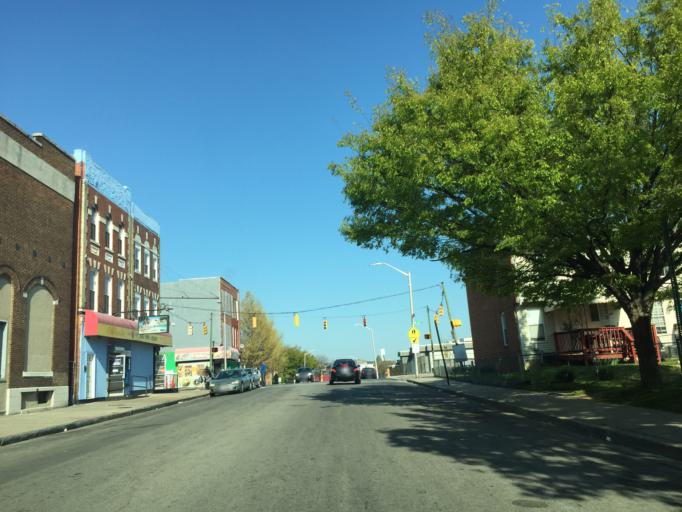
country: US
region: Maryland
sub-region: City of Baltimore
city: Baltimore
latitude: 39.3033
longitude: -76.6396
